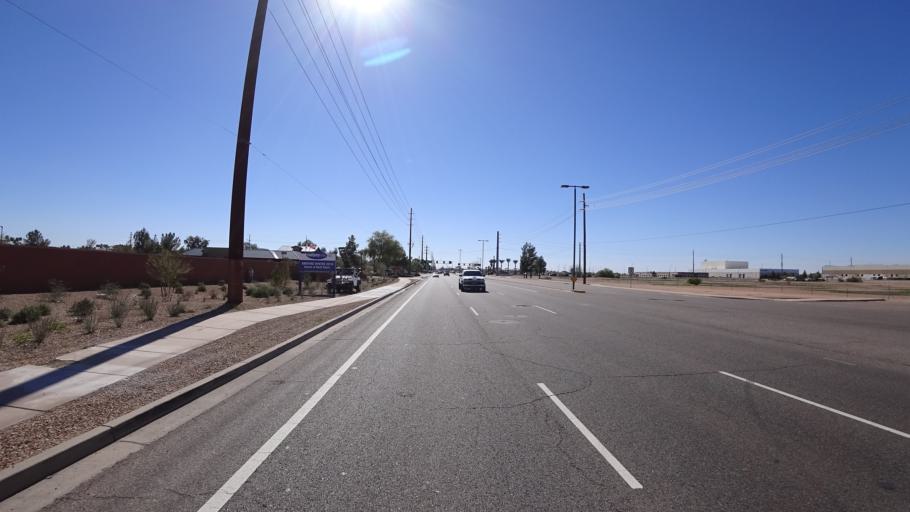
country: US
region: Arizona
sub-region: Maricopa County
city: San Carlos
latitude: 33.3517
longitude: -111.8243
